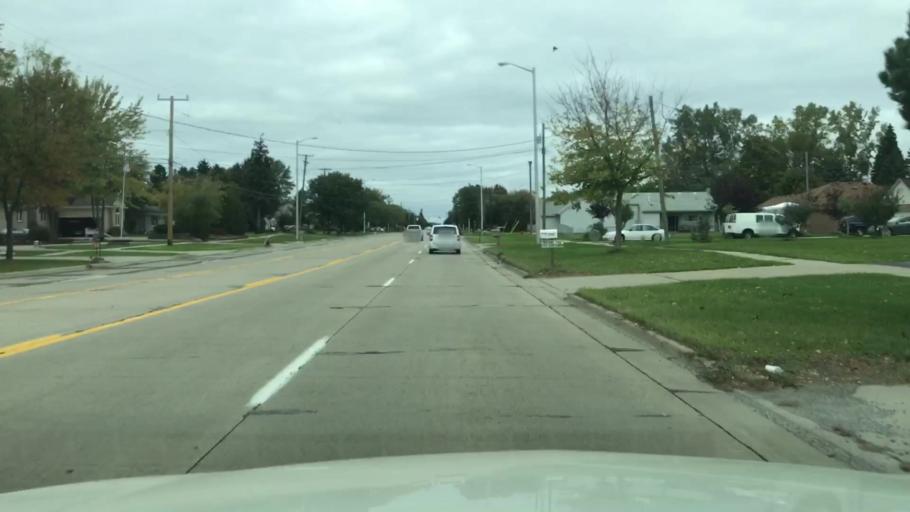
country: US
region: Michigan
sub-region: Macomb County
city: Sterling Heights
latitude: 42.5822
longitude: -83.0703
